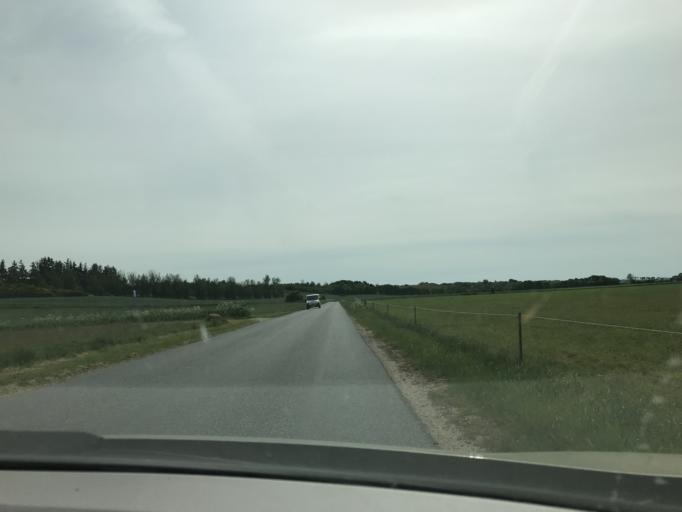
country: DK
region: Central Jutland
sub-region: Norddjurs Kommune
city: Allingabro
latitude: 56.5870
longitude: 10.3105
